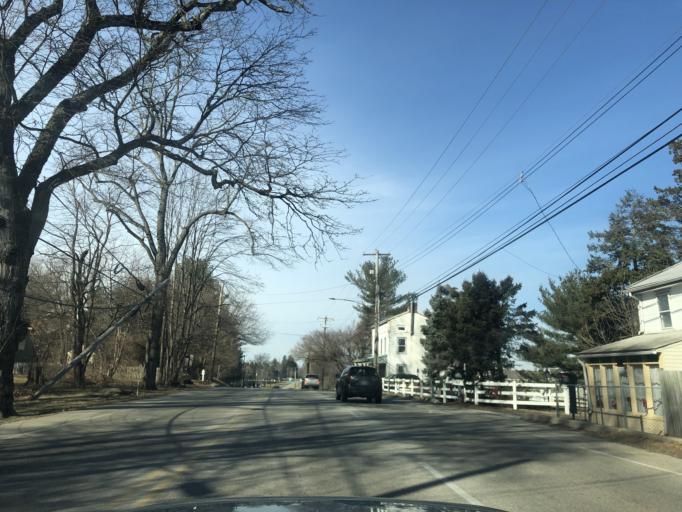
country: US
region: Pennsylvania
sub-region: Montgomery County
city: Plymouth Meeting
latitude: 40.0748
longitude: -75.2448
